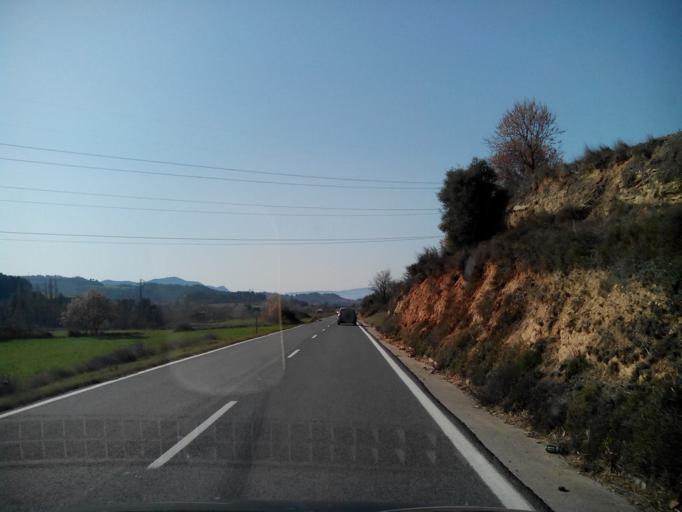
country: ES
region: Catalonia
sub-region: Provincia de Tarragona
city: Fores
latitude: 41.4648
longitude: 1.2697
